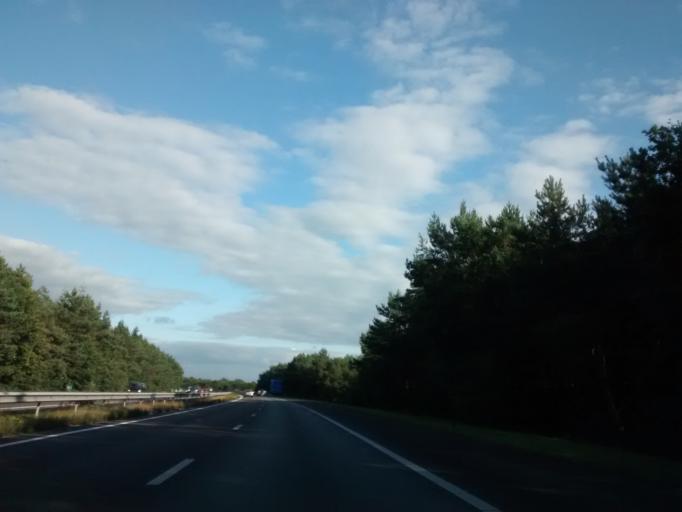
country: NL
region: Gelderland
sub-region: Gemeente Apeldoorn
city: Beekbergen
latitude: 52.1732
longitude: 5.9564
